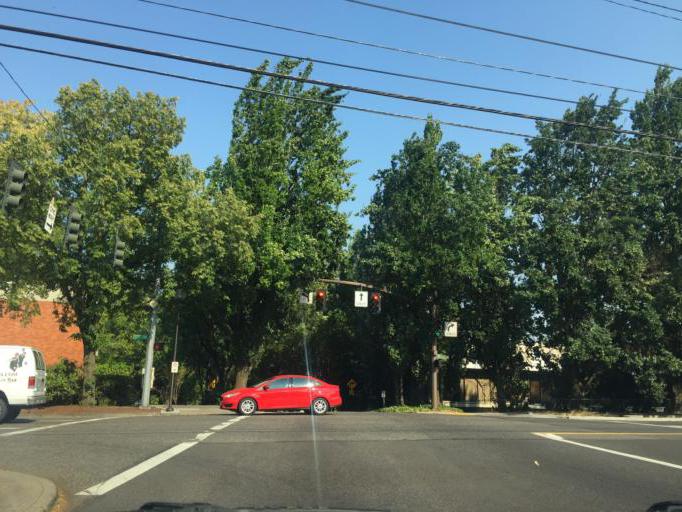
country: US
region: Oregon
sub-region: Multnomah County
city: Portland
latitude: 45.5052
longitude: -122.6823
